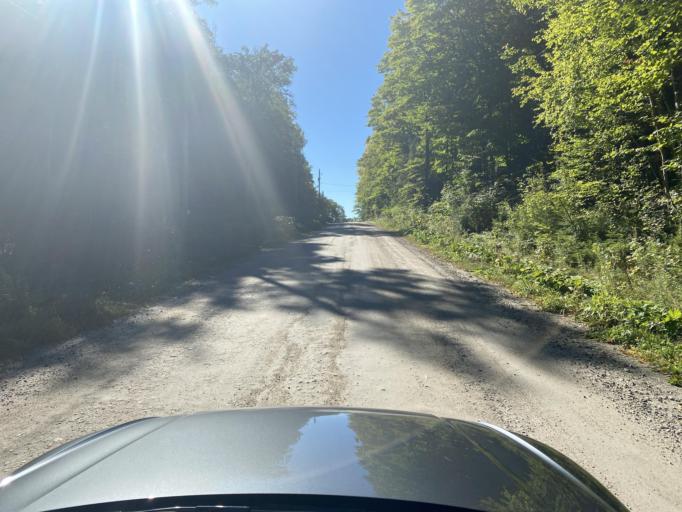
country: CA
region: Quebec
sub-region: Outaouais
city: Wakefield
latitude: 45.6404
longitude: -75.9084
